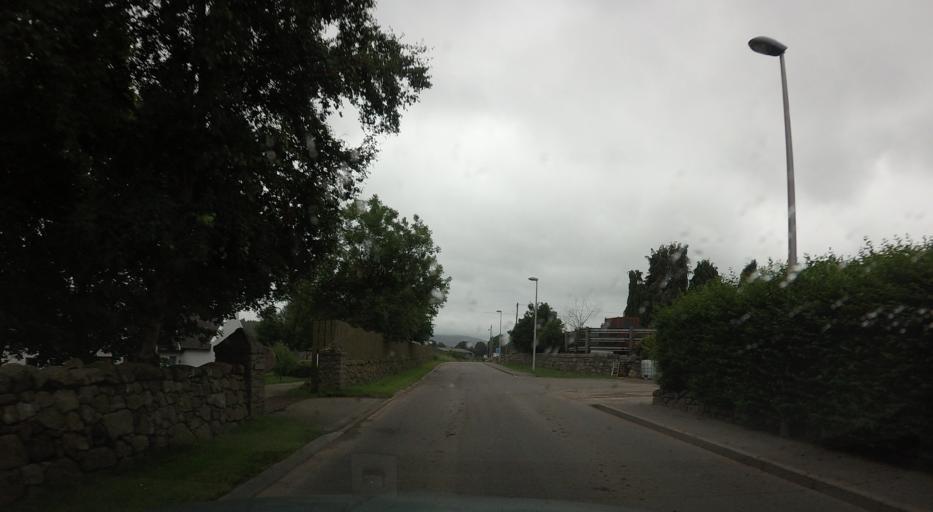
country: GB
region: Scotland
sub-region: Aberdeenshire
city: Banchory
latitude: 57.0216
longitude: -2.5319
